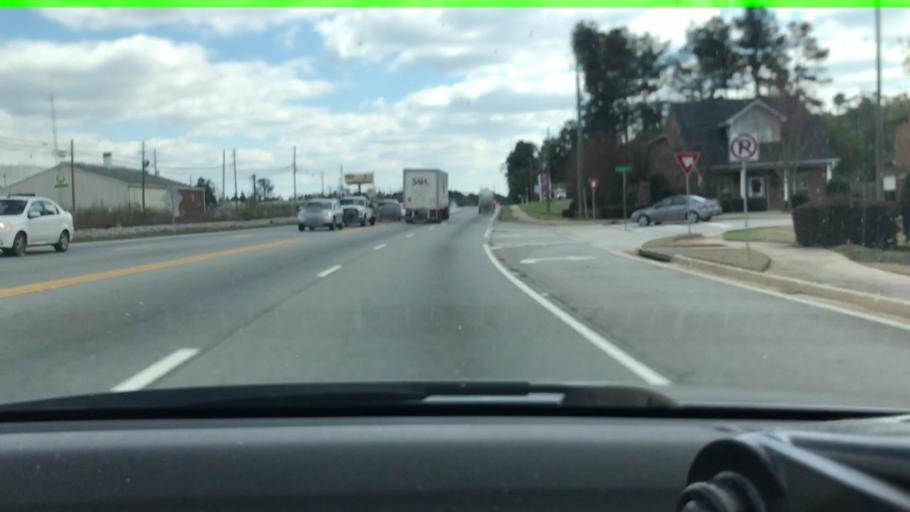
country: US
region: Georgia
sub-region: Clarke County
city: Country Club Estates
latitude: 33.9877
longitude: -83.4219
